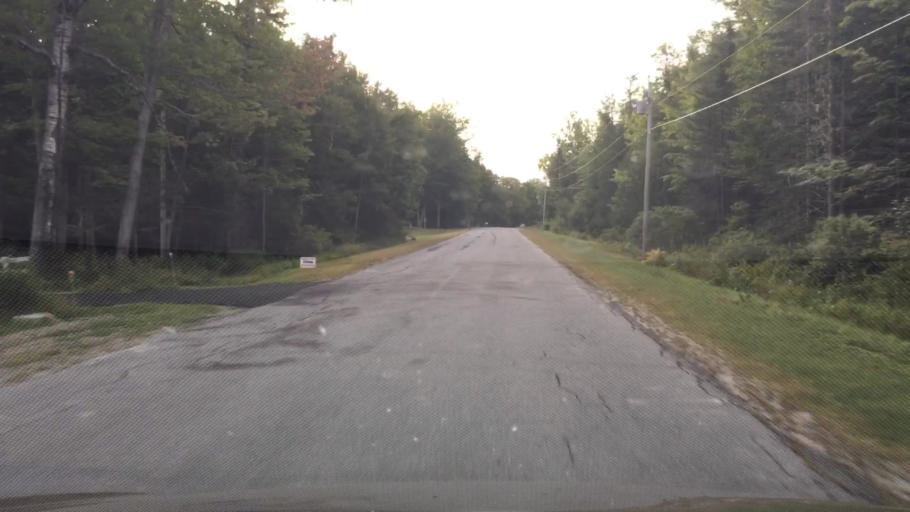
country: US
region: Maine
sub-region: Waldo County
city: Stockton Springs
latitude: 44.4933
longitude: -68.8716
